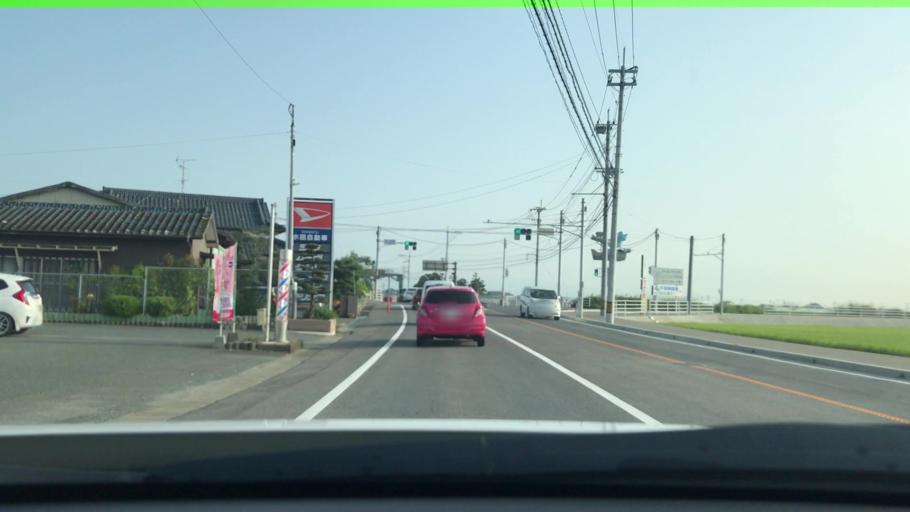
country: JP
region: Saga Prefecture
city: Saga-shi
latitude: 33.2030
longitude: 130.2047
